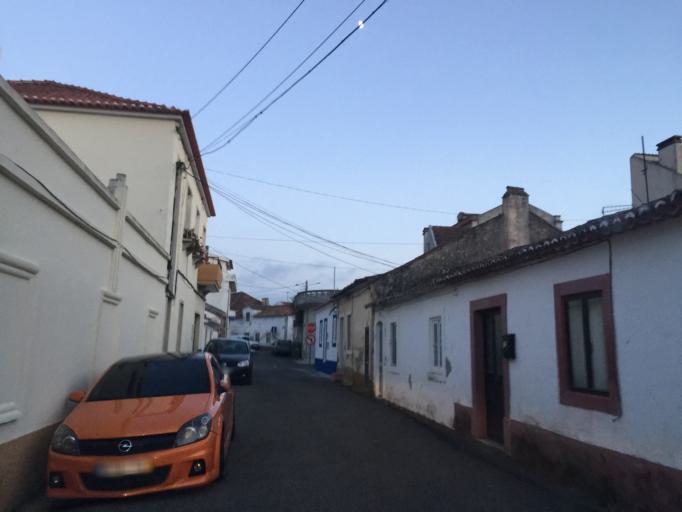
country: PT
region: Leiria
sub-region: Bombarral
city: Bombarral
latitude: 39.2674
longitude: -9.1597
